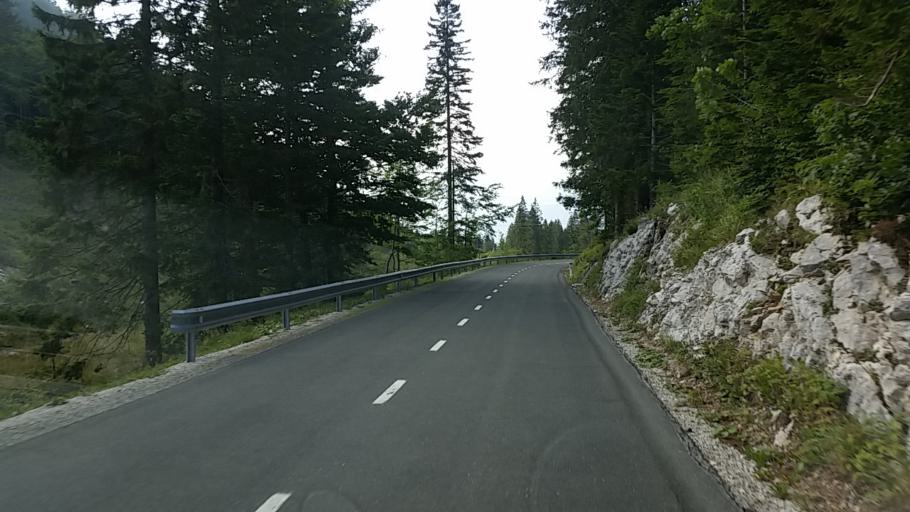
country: SI
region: Bohinj
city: Bohinjska Bistrica
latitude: 46.2451
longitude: 14.0065
